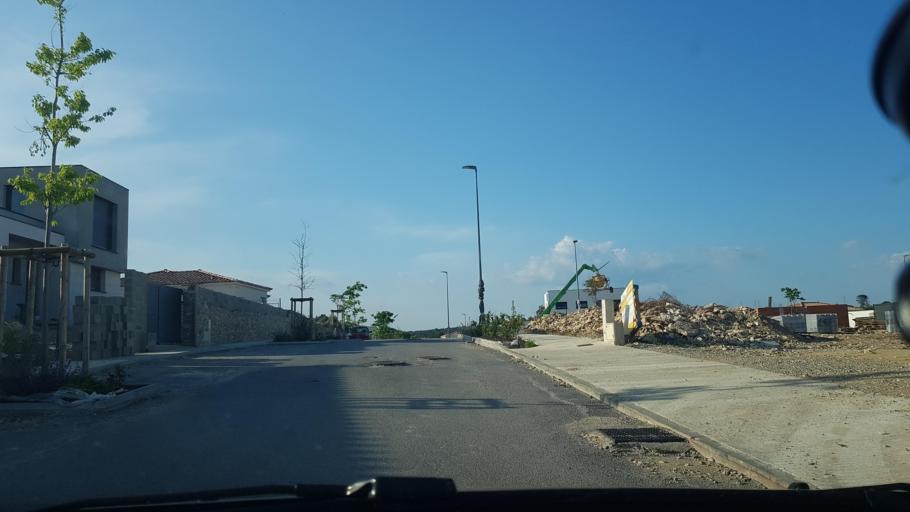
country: FR
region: Languedoc-Roussillon
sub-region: Departement du Gard
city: Caveirac
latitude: 43.8408
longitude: 4.2987
